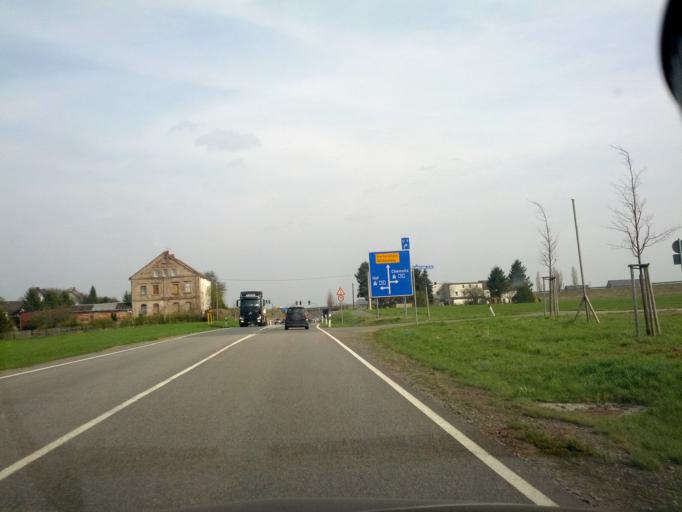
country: DE
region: Saxony
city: Reinsdorf
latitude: 50.6829
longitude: 12.5780
